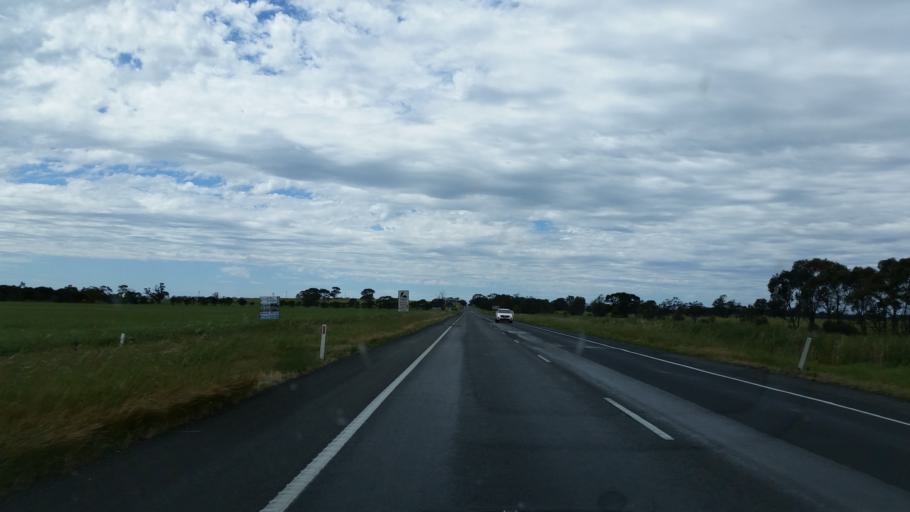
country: AU
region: South Australia
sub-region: Tatiara
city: Bordertown
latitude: -36.3458
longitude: 140.9762
